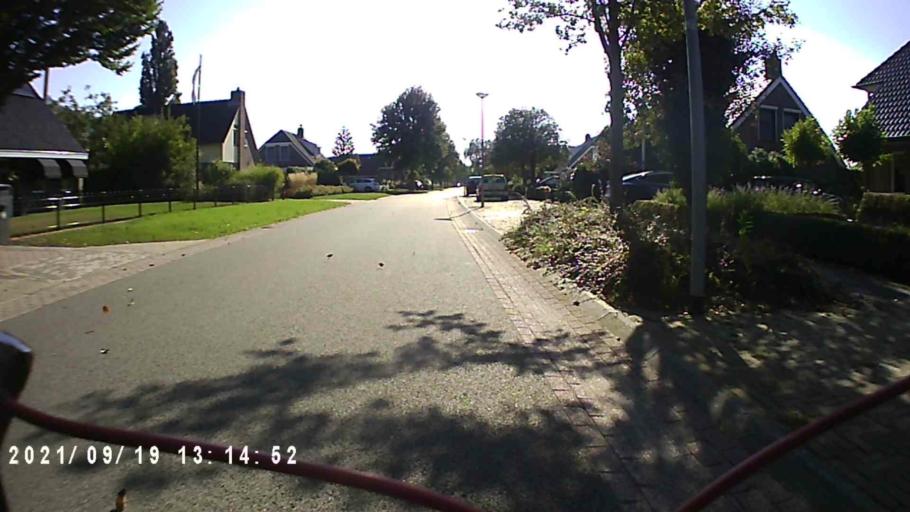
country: NL
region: Groningen
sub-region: Gemeente  Oldambt
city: Winschoten
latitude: 53.1599
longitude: 6.9904
